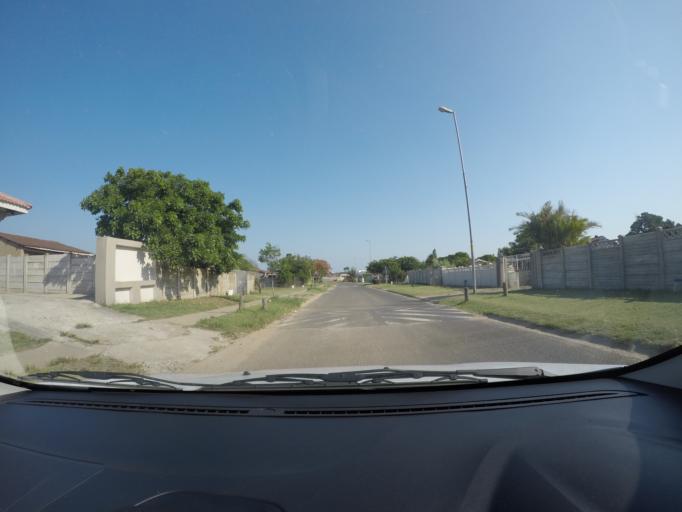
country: ZA
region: KwaZulu-Natal
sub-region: uThungulu District Municipality
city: Richards Bay
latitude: -28.7143
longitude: 32.0334
